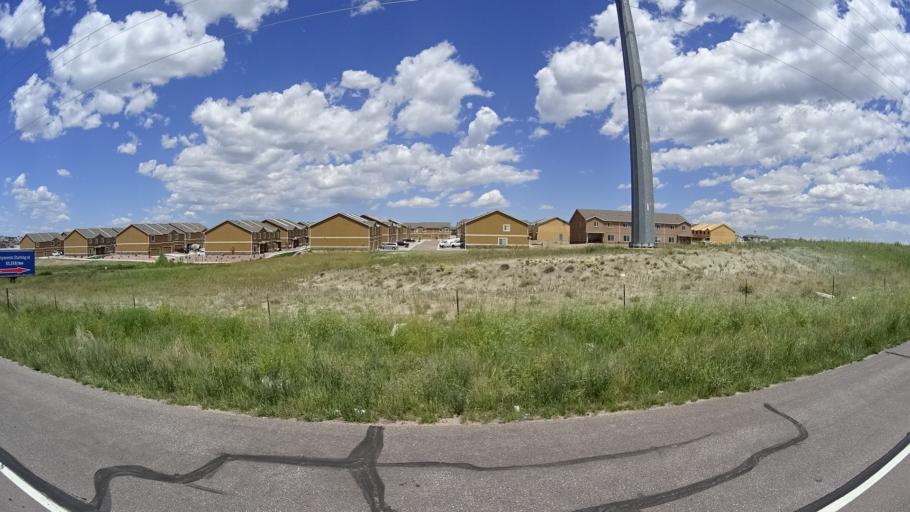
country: US
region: Colorado
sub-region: El Paso County
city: Black Forest
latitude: 38.9411
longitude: -104.6914
